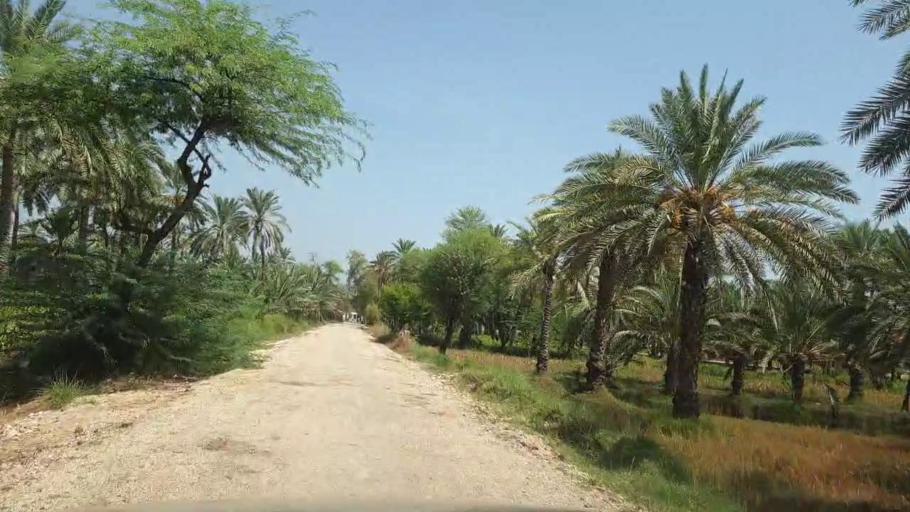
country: PK
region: Sindh
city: Rohri
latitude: 27.6946
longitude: 68.9471
